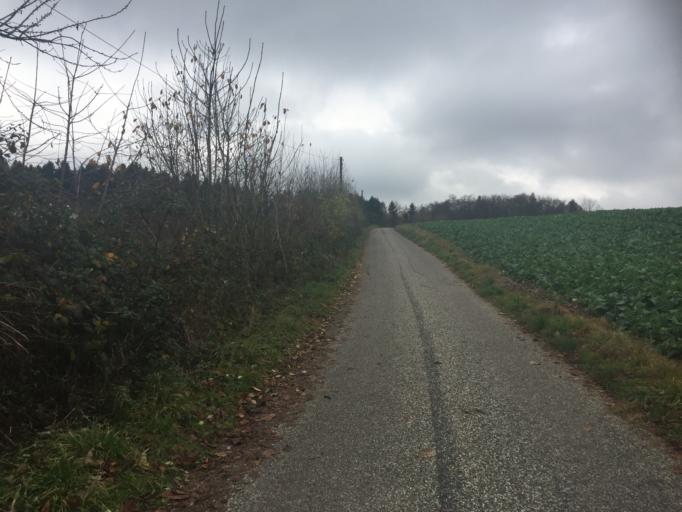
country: DE
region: Baden-Wuerttemberg
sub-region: Karlsruhe Region
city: Zwingenberg
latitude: 49.4333
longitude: 9.0638
